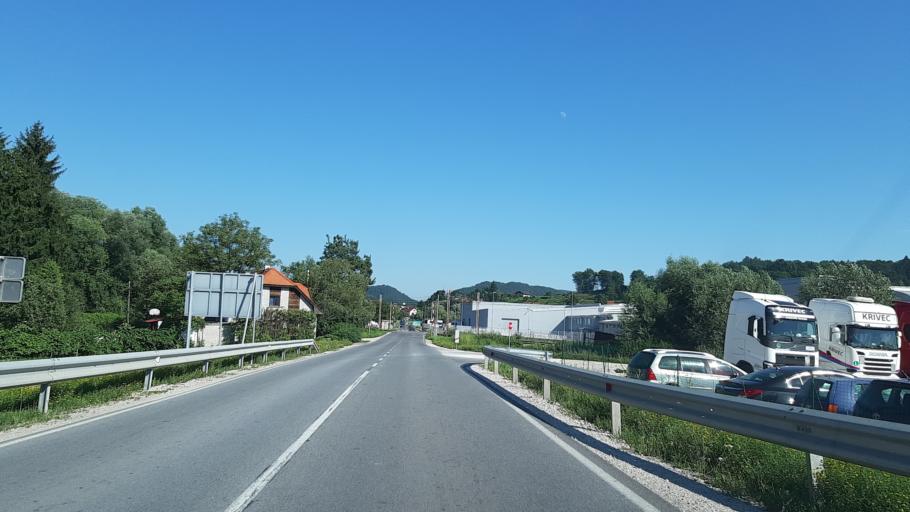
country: SI
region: Sentjur pri Celju
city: Sentjur
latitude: 46.2130
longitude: 15.4033
